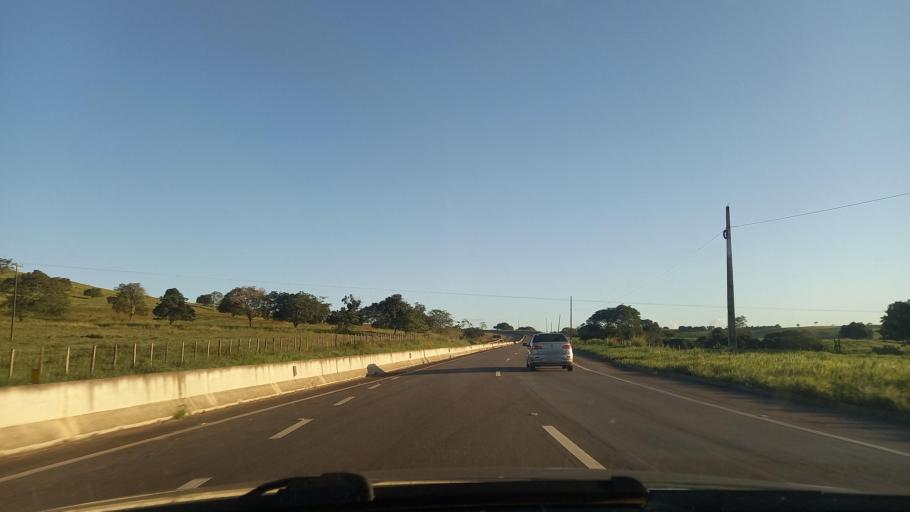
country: BR
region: Alagoas
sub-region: Limoeiro De Anadia
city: Limoeiro de Anadia
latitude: -9.7464
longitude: -36.5018
